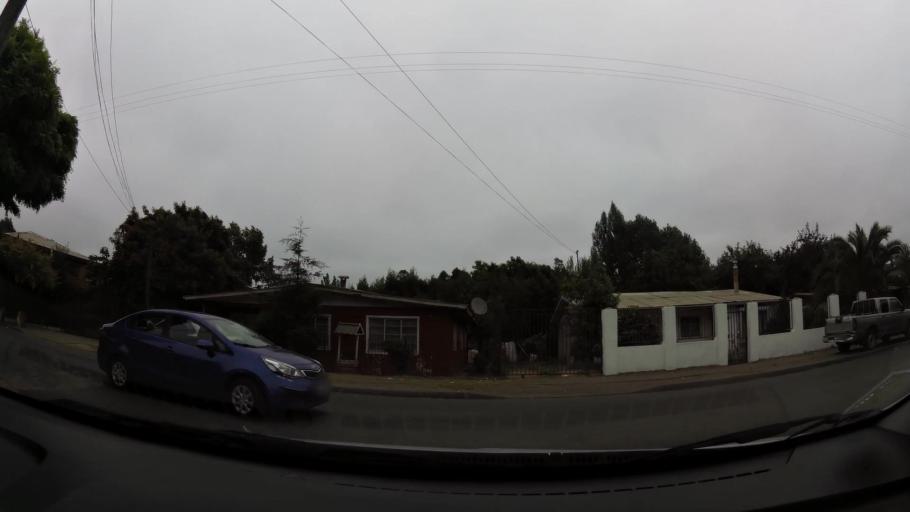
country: CL
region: Biobio
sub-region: Provincia de Concepcion
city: Concepcion
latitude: -36.8344
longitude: -73.0023
